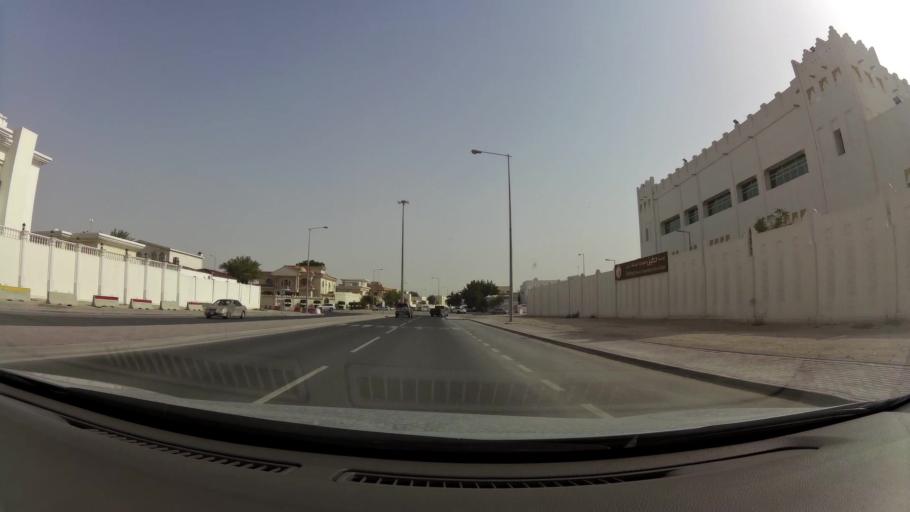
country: QA
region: Baladiyat ar Rayyan
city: Ar Rayyan
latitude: 25.2500
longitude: 51.4426
